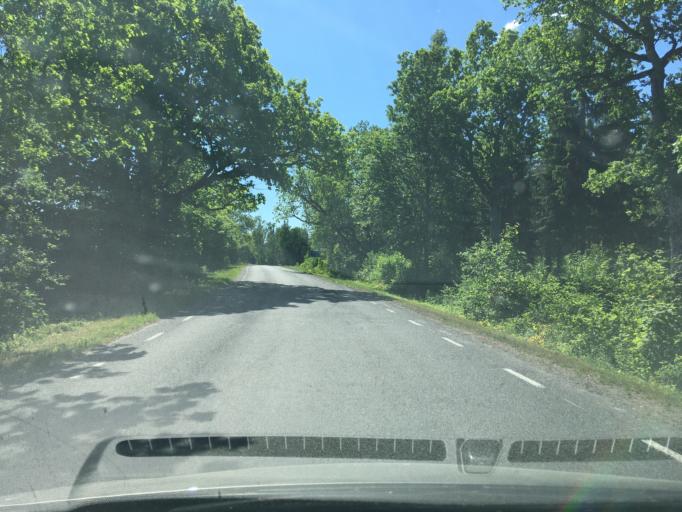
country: EE
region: Raplamaa
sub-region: Kohila vald
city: Kohila
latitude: 59.1228
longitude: 24.8370
